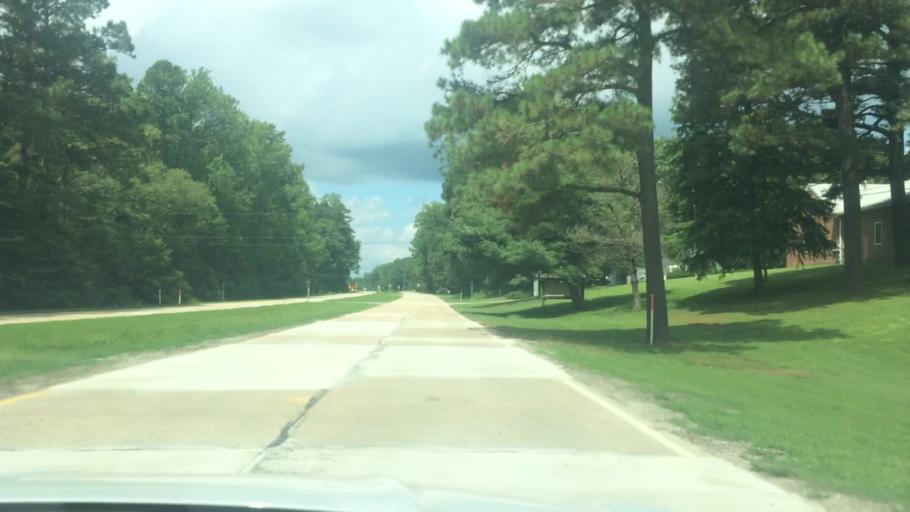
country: US
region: Virginia
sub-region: New Kent County
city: New Kent
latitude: 37.4400
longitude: -77.0290
